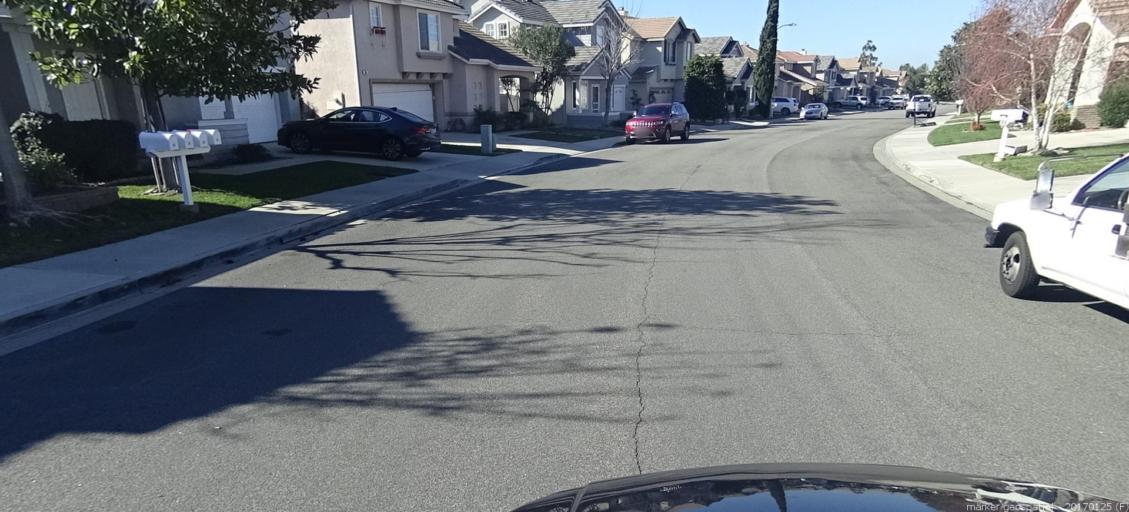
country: US
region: California
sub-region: Orange County
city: Foothill Ranch
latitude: 33.6796
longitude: -117.6491
